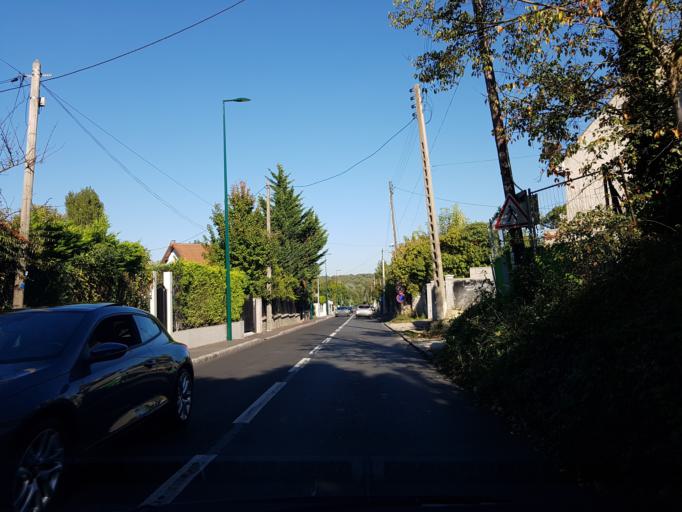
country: FR
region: Ile-de-France
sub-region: Departement du Val-de-Marne
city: Sucy-en-Brie
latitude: 48.7729
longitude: 2.5295
